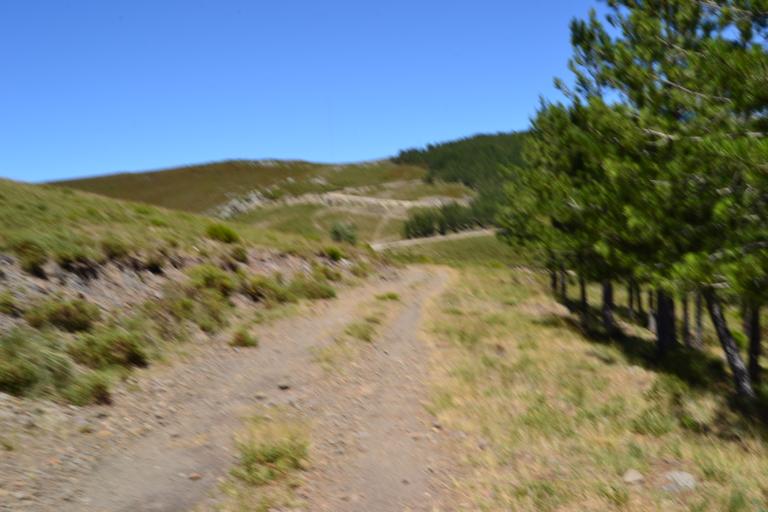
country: PT
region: Vila Real
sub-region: Mesao Frio
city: Mesao Frio
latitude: 41.2387
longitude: -7.9022
